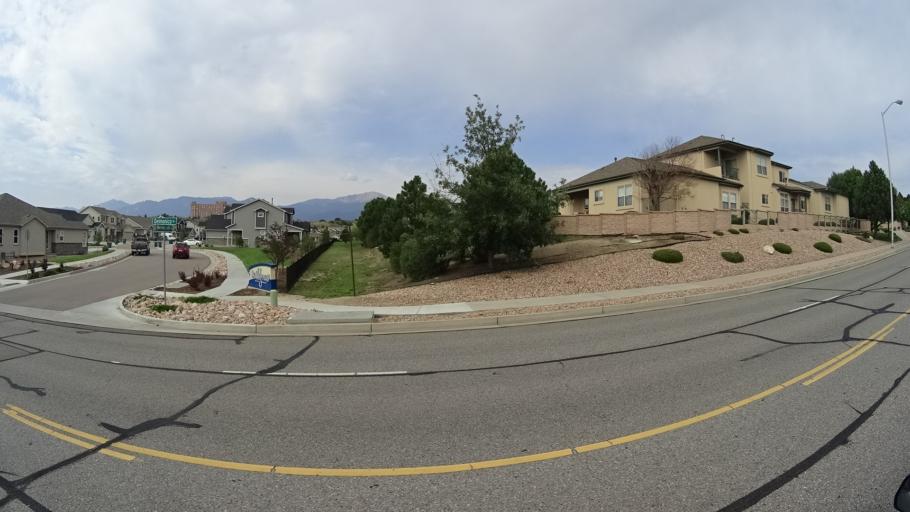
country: US
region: Colorado
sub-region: El Paso County
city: Colorado Springs
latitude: 38.9178
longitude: -104.8245
